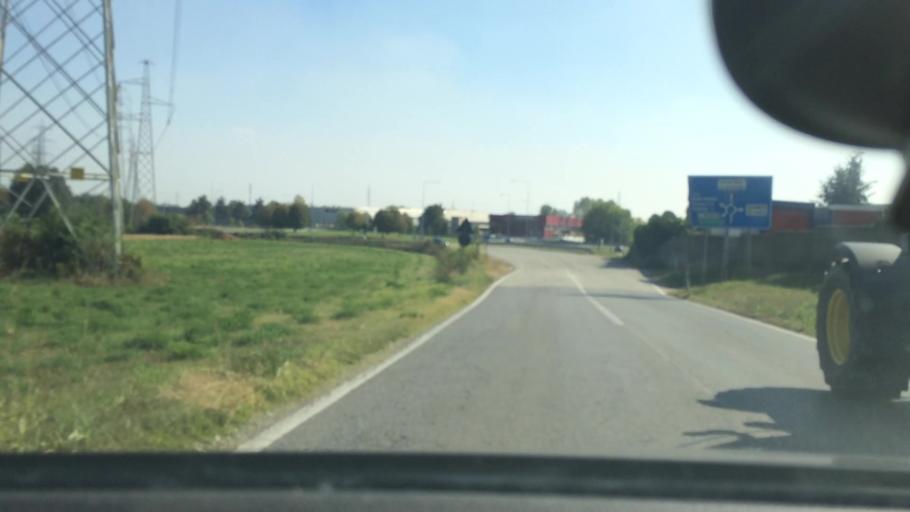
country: IT
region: Lombardy
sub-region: Citta metropolitana di Milano
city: Casate
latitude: 45.4833
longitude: 8.8305
